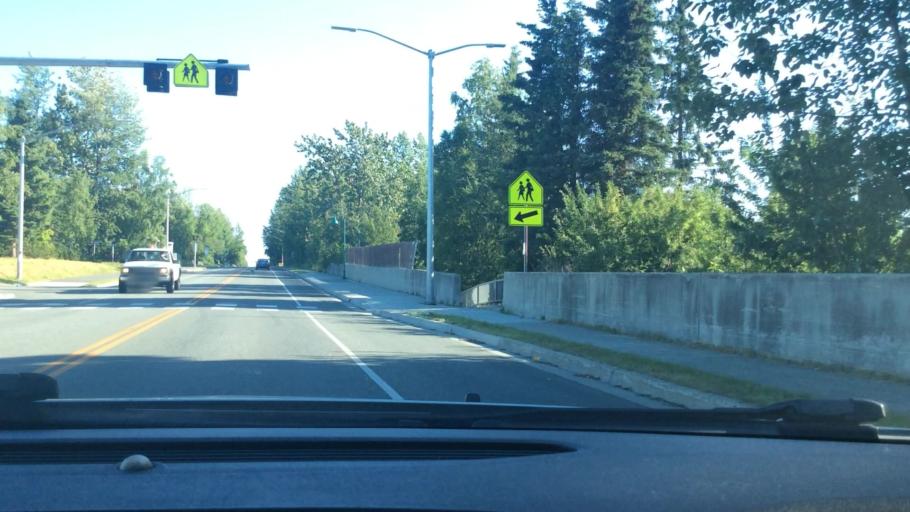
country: US
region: Alaska
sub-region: Anchorage Municipality
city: Anchorage
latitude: 61.1937
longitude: -149.7634
